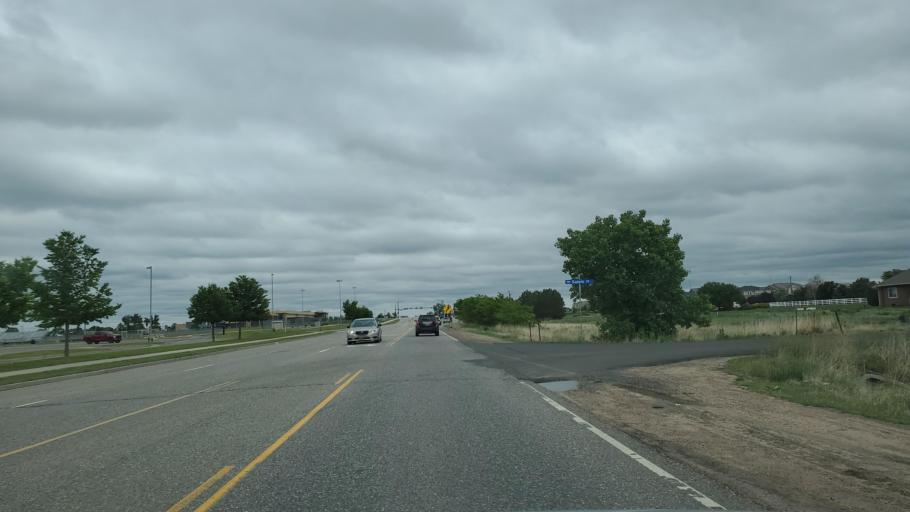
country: US
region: Colorado
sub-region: Adams County
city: Todd Creek
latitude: 39.9144
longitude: -104.8405
